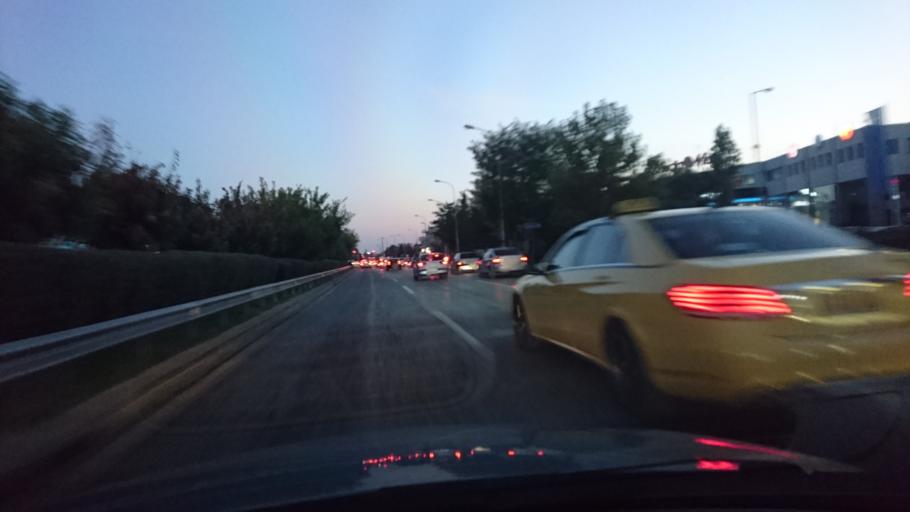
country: GR
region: Attica
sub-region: Nomarchia Athinas
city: Argyroupoli
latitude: 37.9146
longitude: 23.7444
